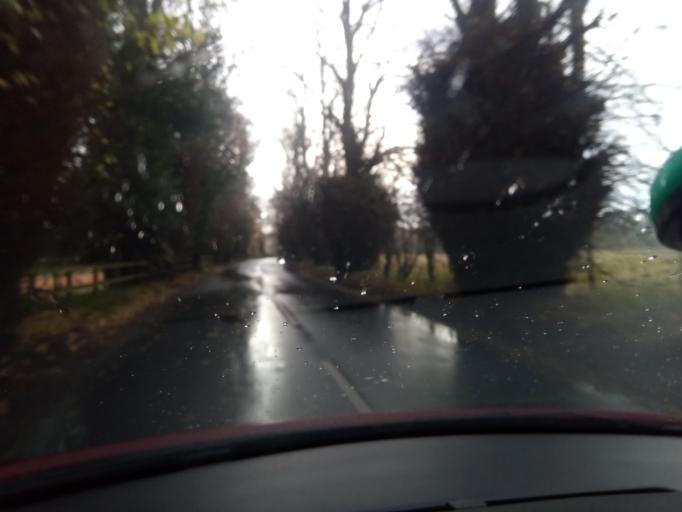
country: GB
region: England
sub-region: Northumberland
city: Birtley
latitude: 55.0984
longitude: -2.2240
